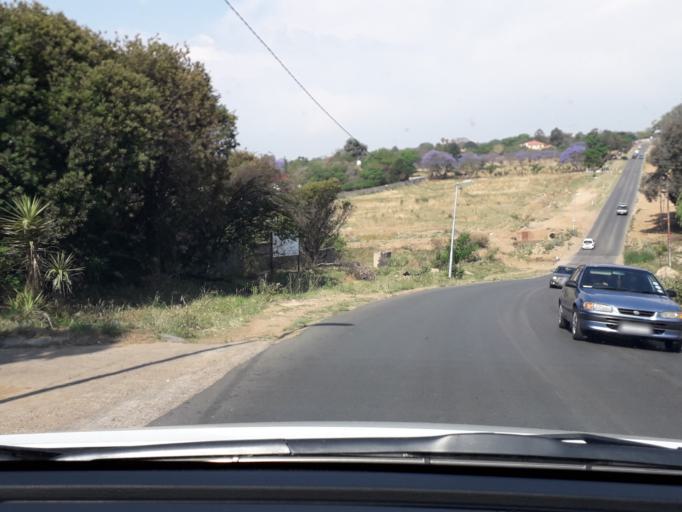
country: ZA
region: Gauteng
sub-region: West Rand District Municipality
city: Muldersdriseloop
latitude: -26.0514
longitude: 27.9368
